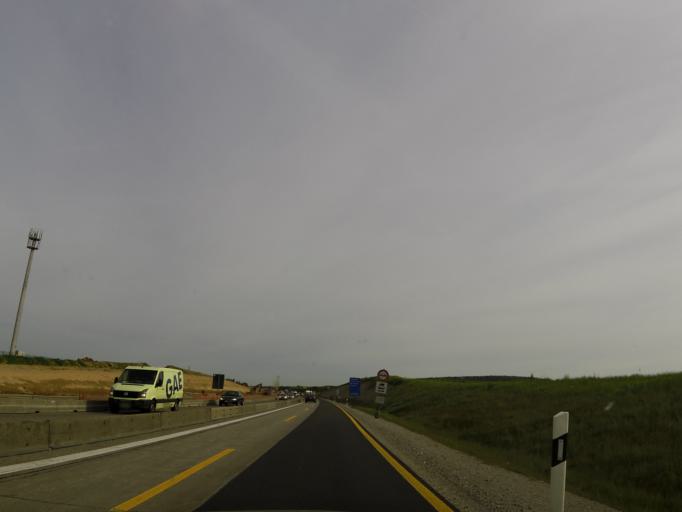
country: DE
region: Lower Saxony
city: Seesen
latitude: 51.9393
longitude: 10.1456
